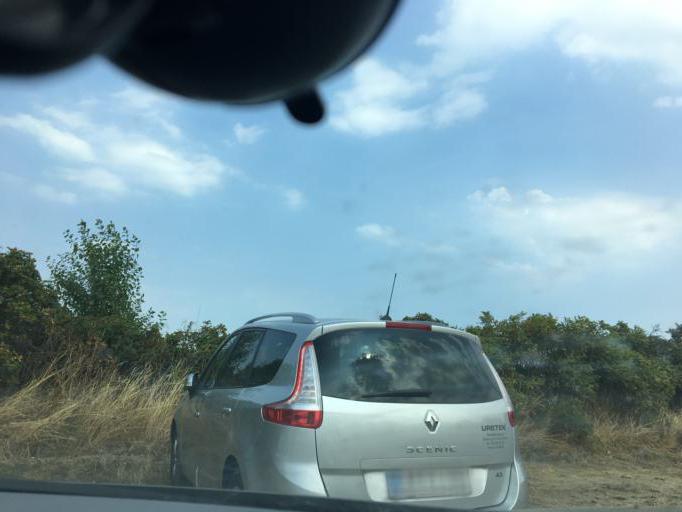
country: DK
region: South Denmark
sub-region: Middelfart Kommune
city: Norre Aby
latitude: 55.5102
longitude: 9.8823
